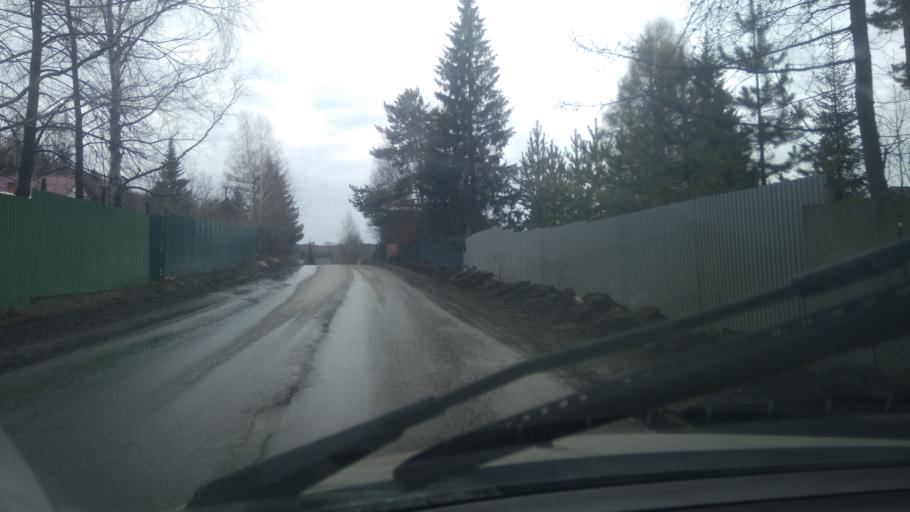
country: RU
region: Sverdlovsk
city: Severka
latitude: 56.8475
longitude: 60.3833
